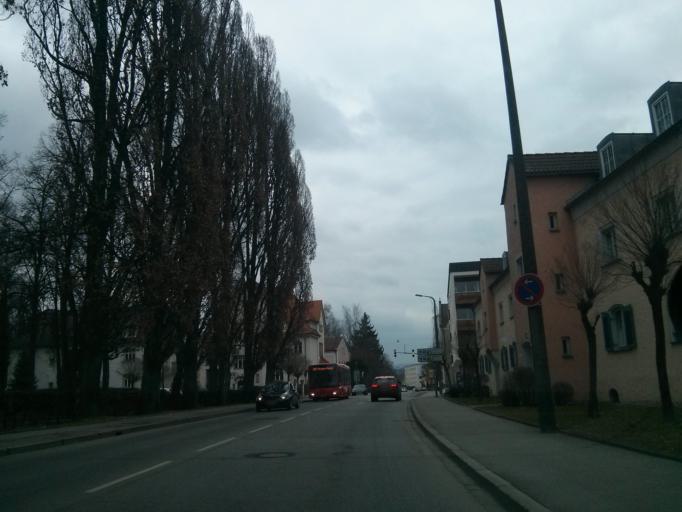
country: DE
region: Bavaria
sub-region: Lower Bavaria
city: Deggendorf
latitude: 48.8330
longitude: 12.9581
